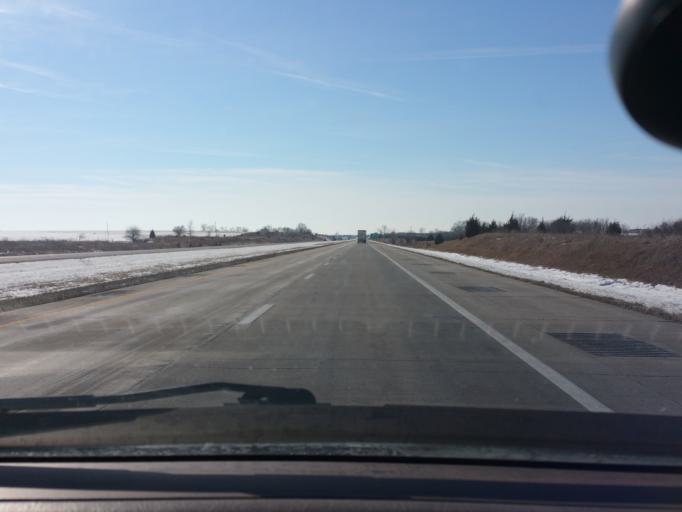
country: US
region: Missouri
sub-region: Harrison County
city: Bethany
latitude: 40.1746
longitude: -94.0189
